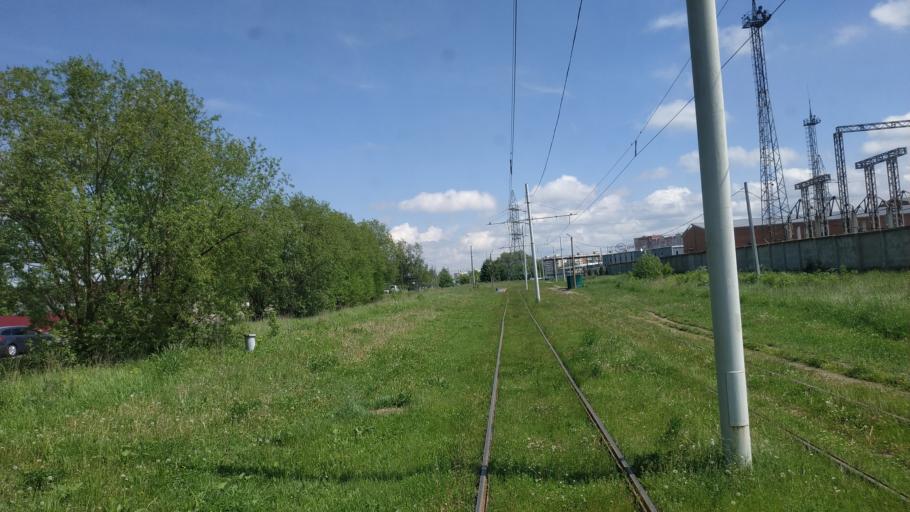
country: RU
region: Moskovskaya
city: Sychevo
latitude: 55.0598
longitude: 38.7305
